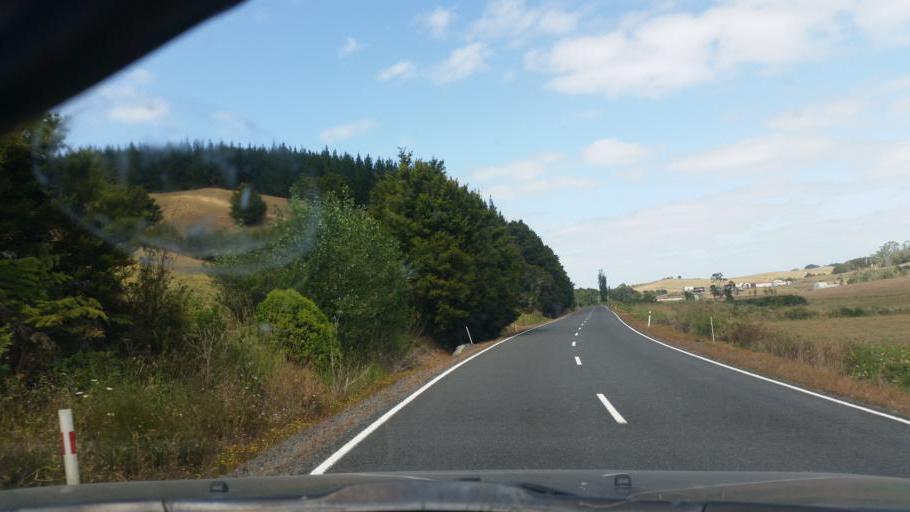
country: NZ
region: Northland
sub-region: Whangarei
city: Ruakaka
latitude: -35.9692
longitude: 174.2900
